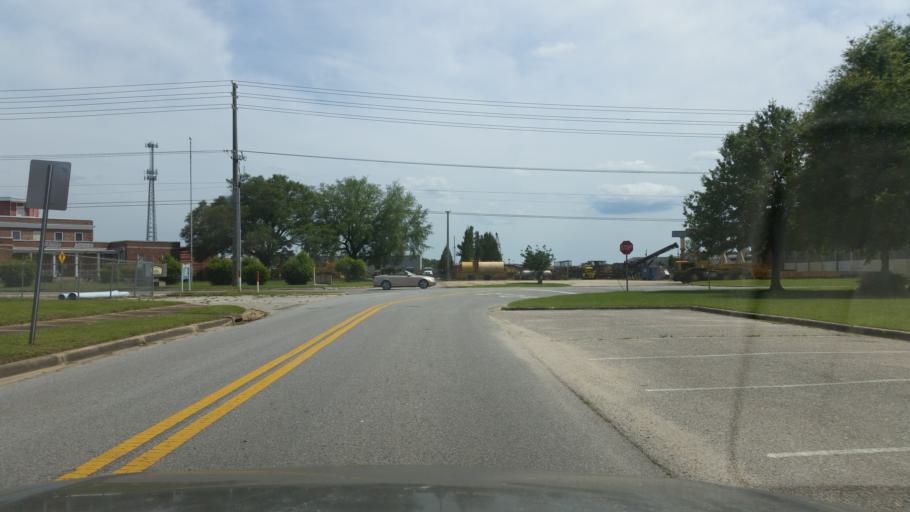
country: US
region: Florida
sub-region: Escambia County
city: Ferry Pass
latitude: 30.5282
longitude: -87.1987
